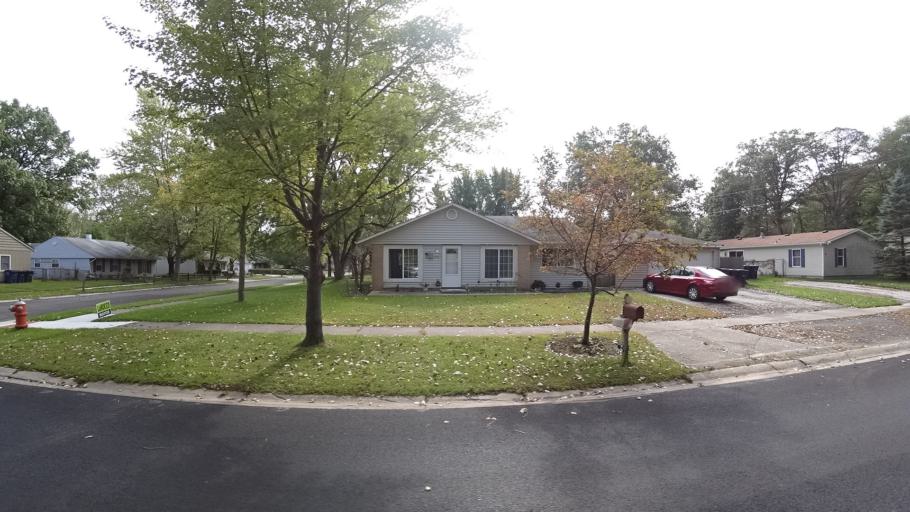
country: US
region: Indiana
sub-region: LaPorte County
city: Long Beach
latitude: 41.7187
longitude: -86.8290
